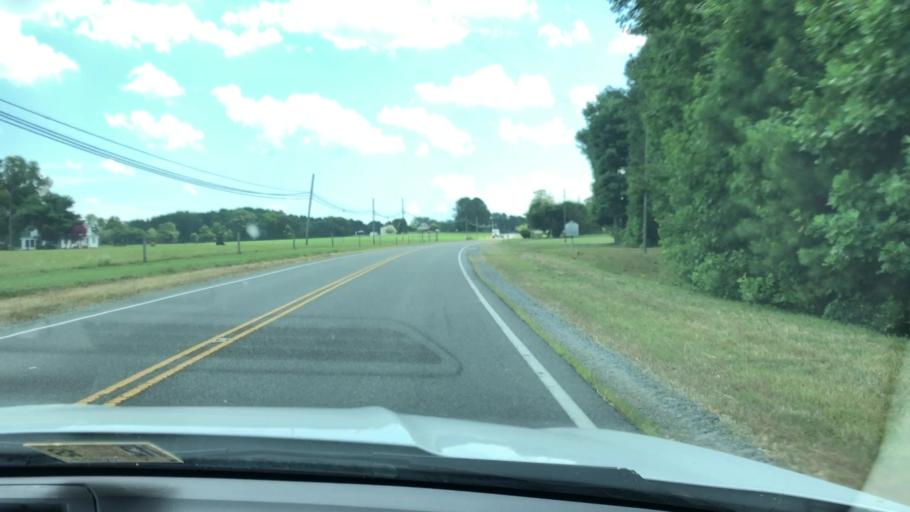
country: US
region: Virginia
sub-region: Lancaster County
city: Lancaster
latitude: 37.7942
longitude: -76.5202
